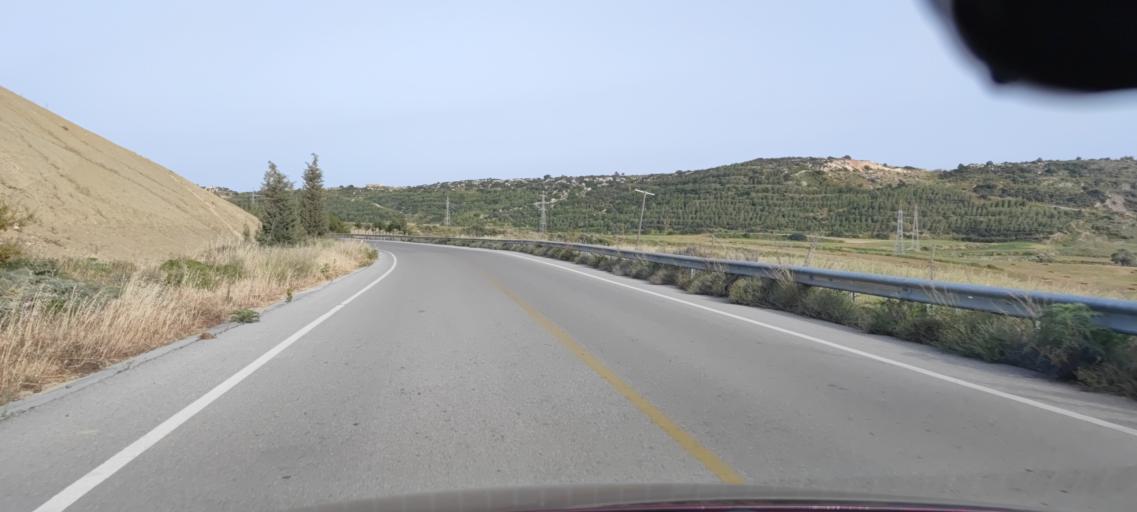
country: CY
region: Ammochostos
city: Leonarisso
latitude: 35.4777
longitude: 34.1282
